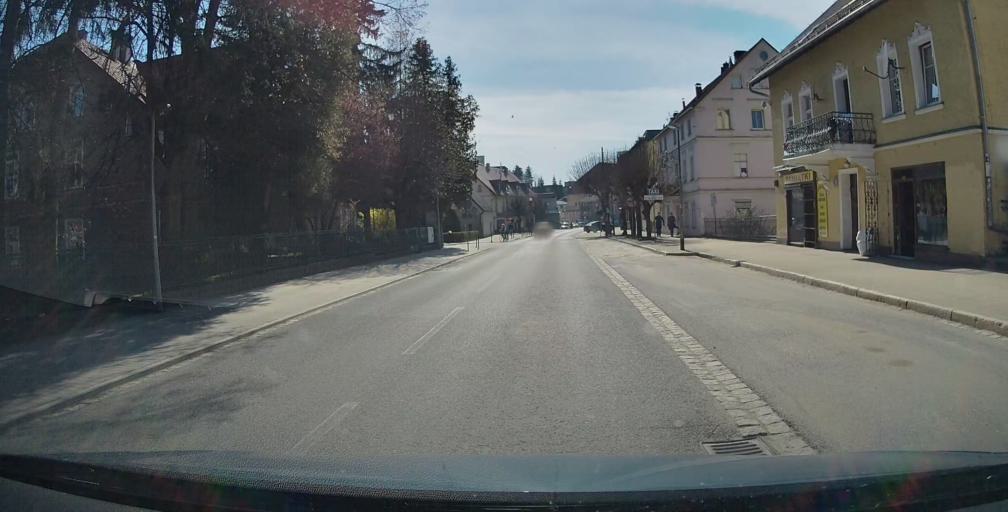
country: PL
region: Lower Silesian Voivodeship
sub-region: Powiat klodzki
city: Kudowa-Zdroj
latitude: 50.4428
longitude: 16.2500
